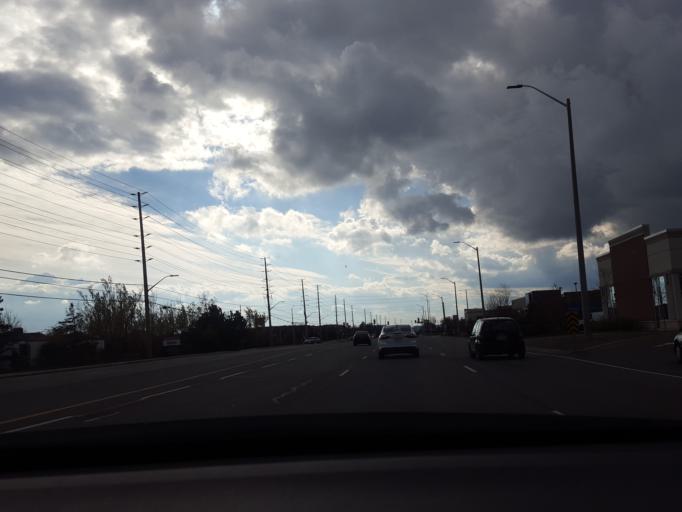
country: CA
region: Ontario
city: Brampton
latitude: 43.6384
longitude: -79.7150
